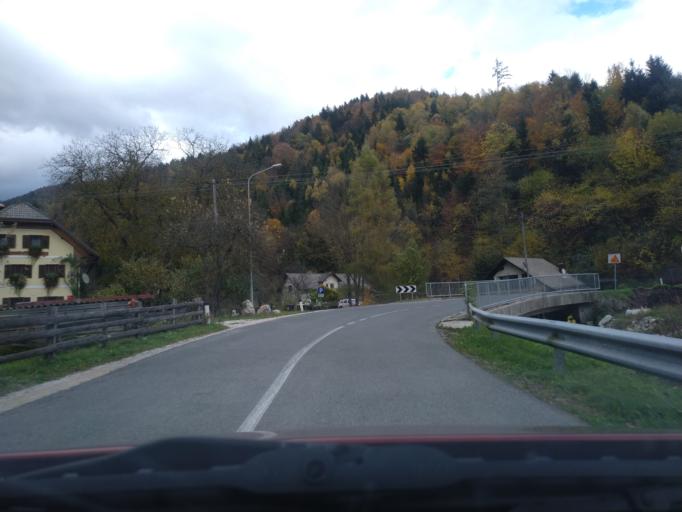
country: SI
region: Kamnik
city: Mekinje
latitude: 46.2637
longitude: 14.6707
